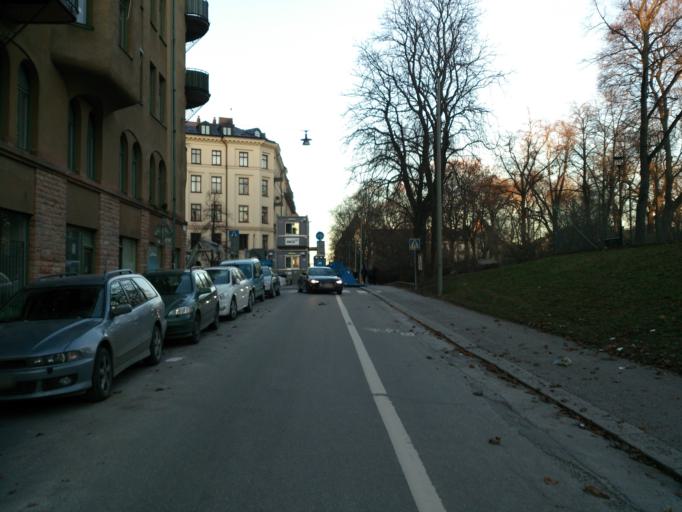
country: SE
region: Stockholm
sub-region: Stockholms Kommun
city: Stockholm
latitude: 59.3316
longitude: 18.0330
